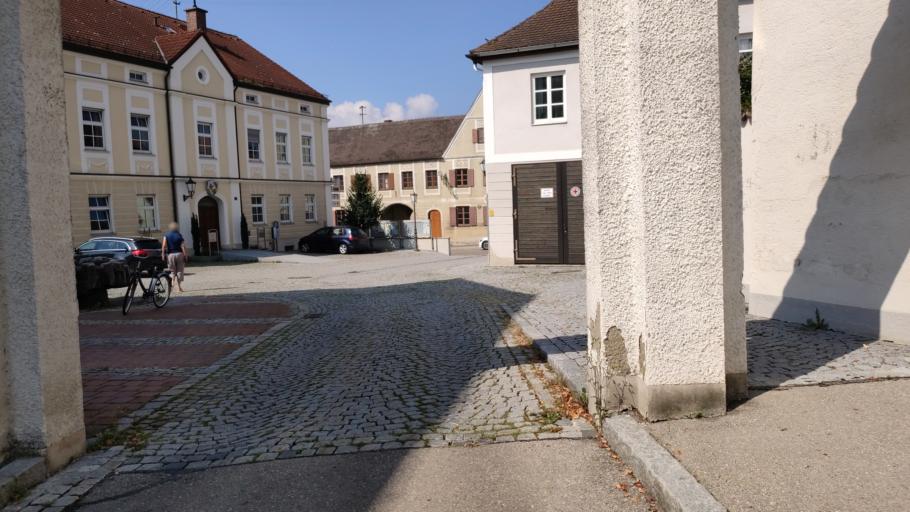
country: DE
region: Bavaria
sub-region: Swabia
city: Grossaitingen
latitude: 48.2283
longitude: 10.7818
